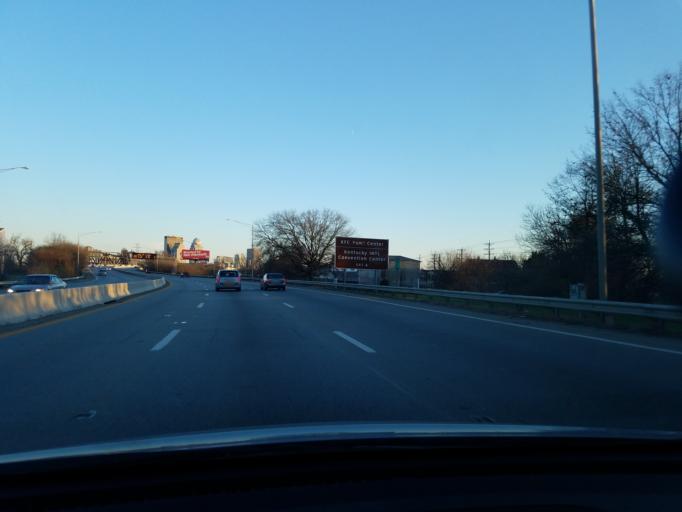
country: US
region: Kentucky
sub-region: Jefferson County
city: Louisville
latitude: 38.2662
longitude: -85.7787
